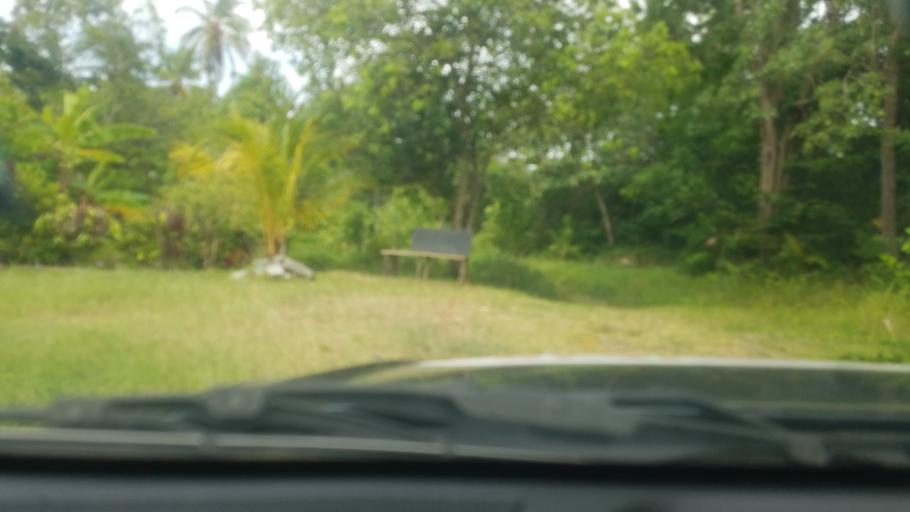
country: LC
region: Micoud Quarter
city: Micoud
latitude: 13.7960
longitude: -60.9315
